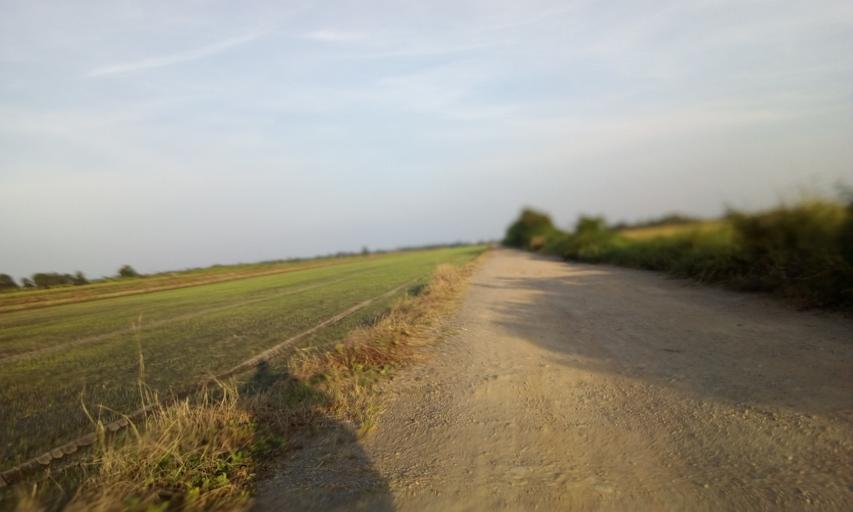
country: TH
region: Pathum Thani
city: Ban Lam Luk Ka
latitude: 14.0354
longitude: 100.8480
